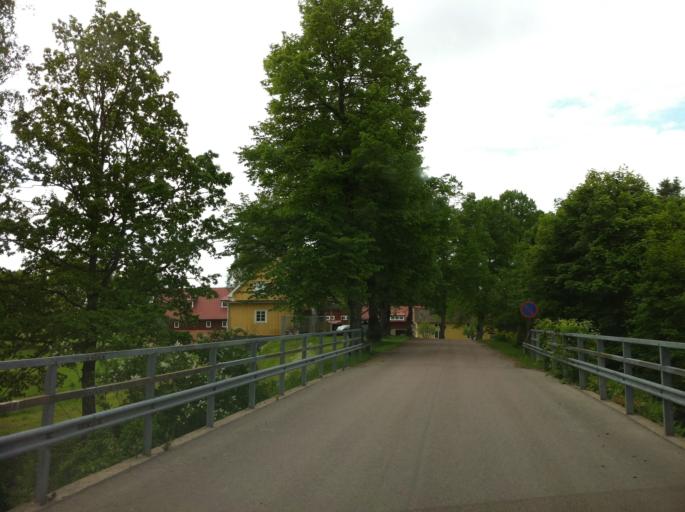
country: SE
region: Vaermland
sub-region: Sunne Kommun
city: Sunne
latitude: 59.9040
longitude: 13.1669
